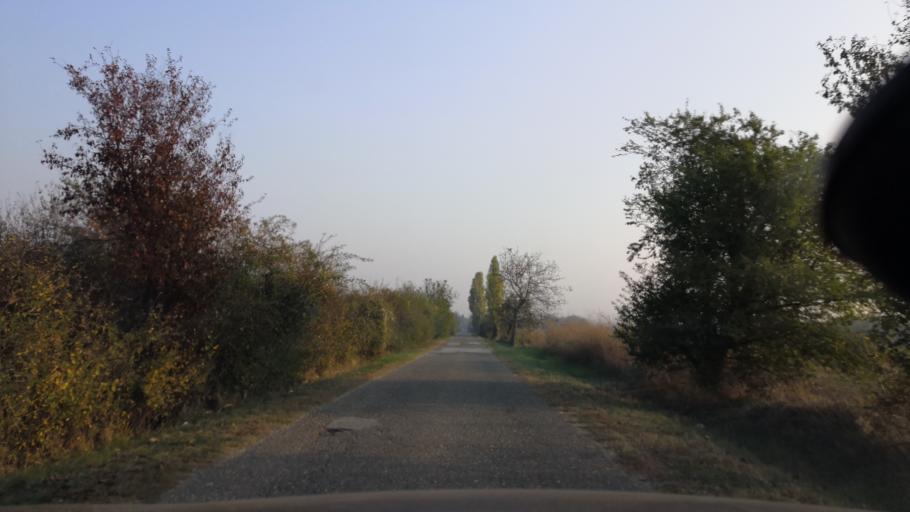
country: RS
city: Cortanovci
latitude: 45.1351
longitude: 19.9858
